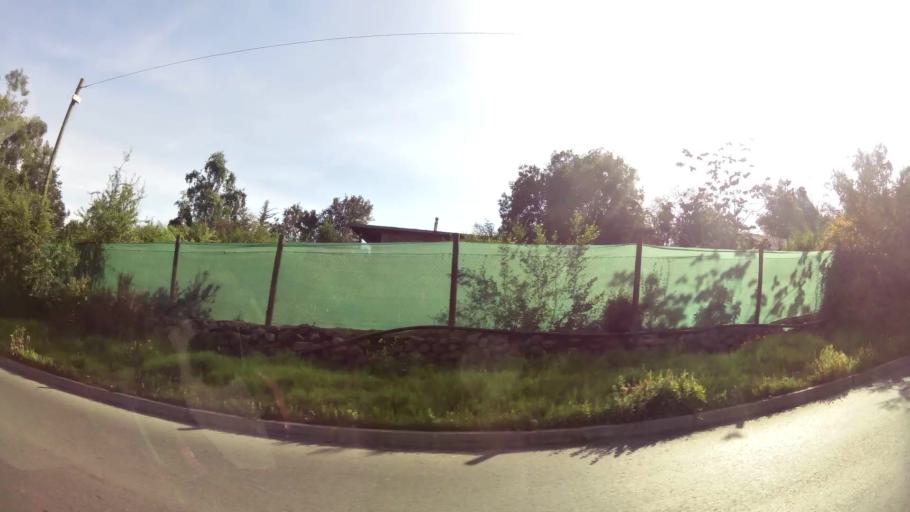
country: CL
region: Santiago Metropolitan
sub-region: Provincia de Santiago
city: Villa Presidente Frei, Nunoa, Santiago, Chile
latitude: -33.4938
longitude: -70.5341
